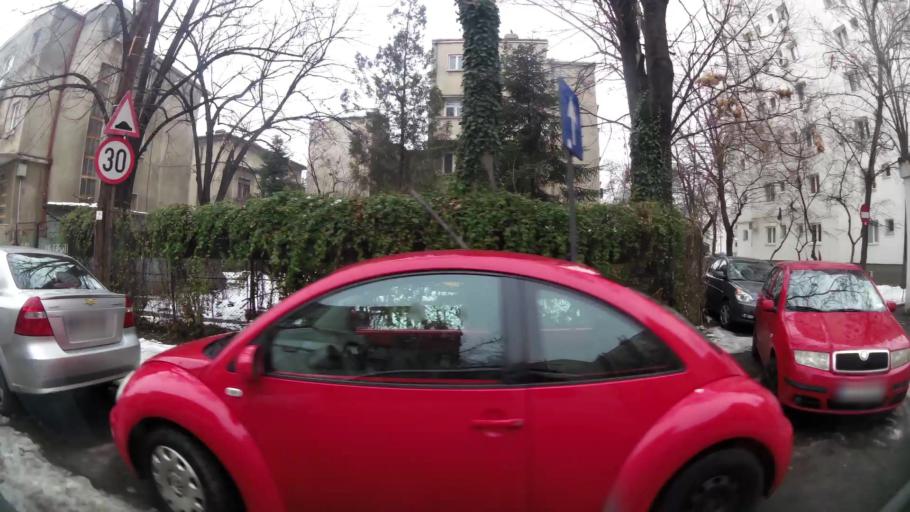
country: RO
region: Bucuresti
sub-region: Municipiul Bucuresti
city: Bucharest
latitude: 44.4281
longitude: 26.1255
